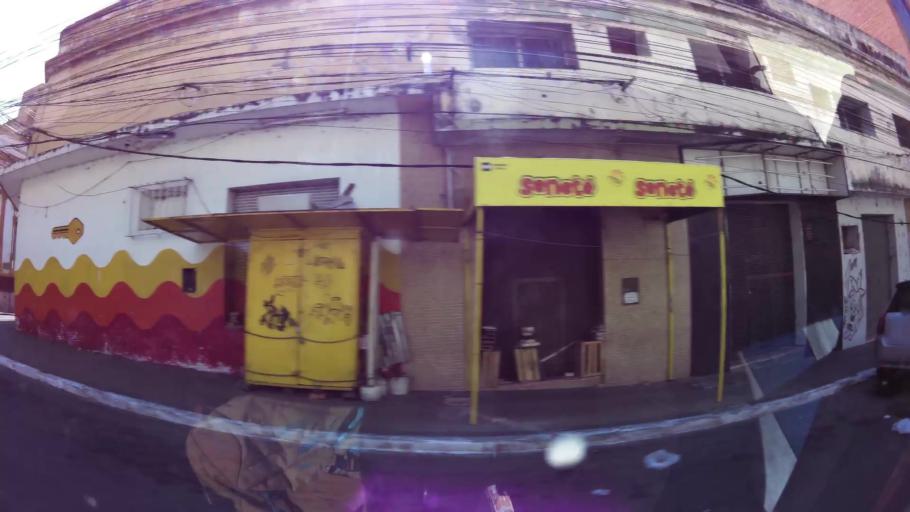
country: PY
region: Asuncion
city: Asuncion
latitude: -25.2811
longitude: -57.6393
